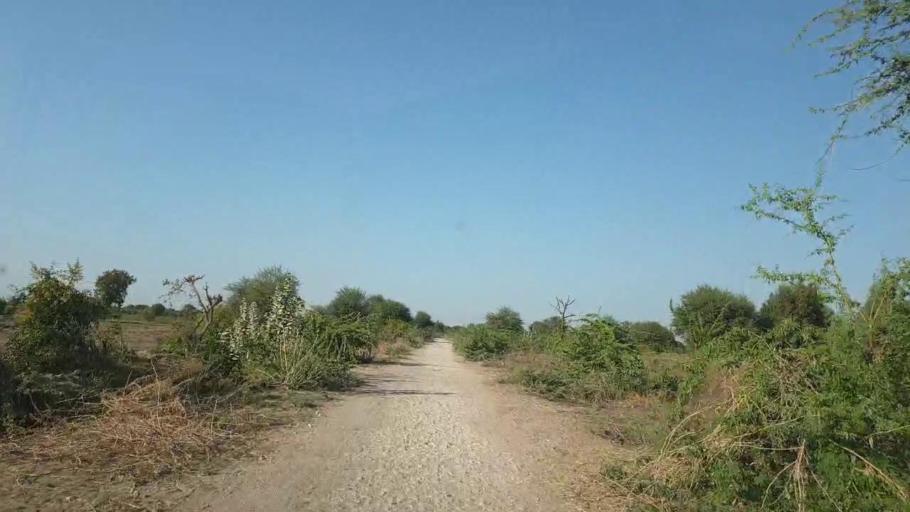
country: PK
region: Sindh
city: Kunri
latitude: 25.0582
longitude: 69.4420
